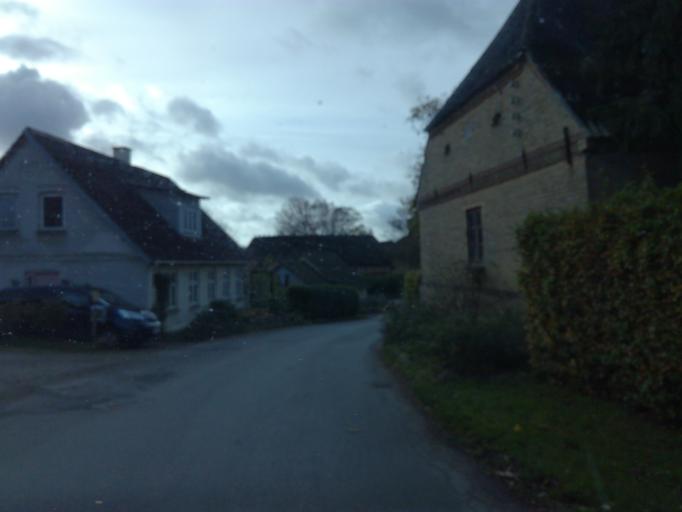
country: DK
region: South Denmark
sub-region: Vejle Kommune
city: Borkop
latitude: 55.6659
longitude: 9.6492
